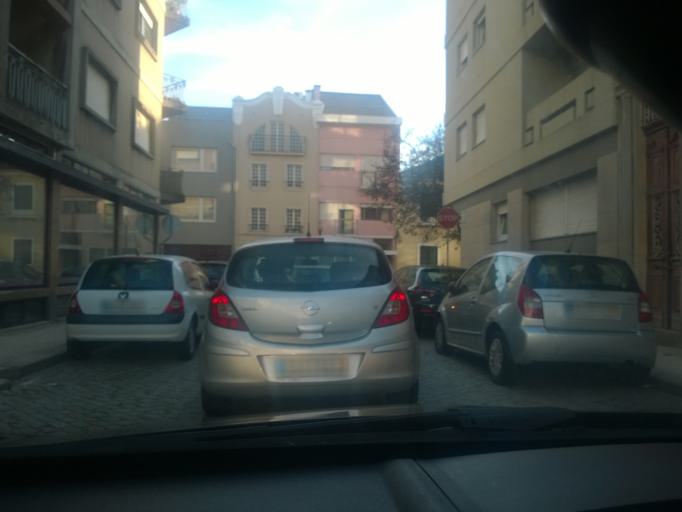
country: PT
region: Porto
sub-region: Porto
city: Porto
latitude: 41.1584
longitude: -8.6372
